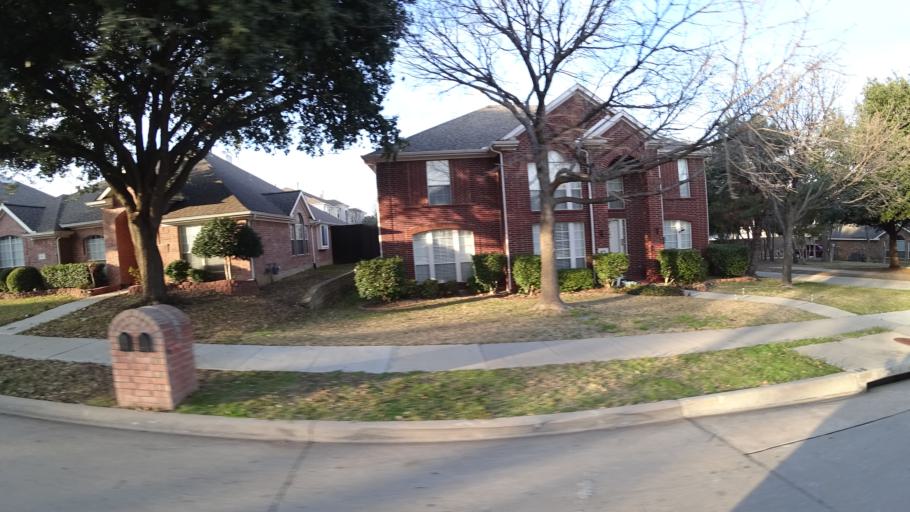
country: US
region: Texas
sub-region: Denton County
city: Lewisville
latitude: 32.9967
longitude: -96.9833
